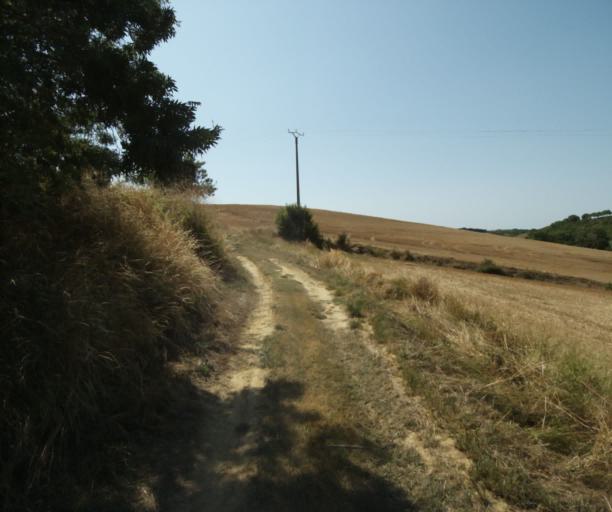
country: FR
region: Midi-Pyrenees
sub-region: Departement de la Haute-Garonne
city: Saint-Felix-Lauragais
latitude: 43.4502
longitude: 1.8733
